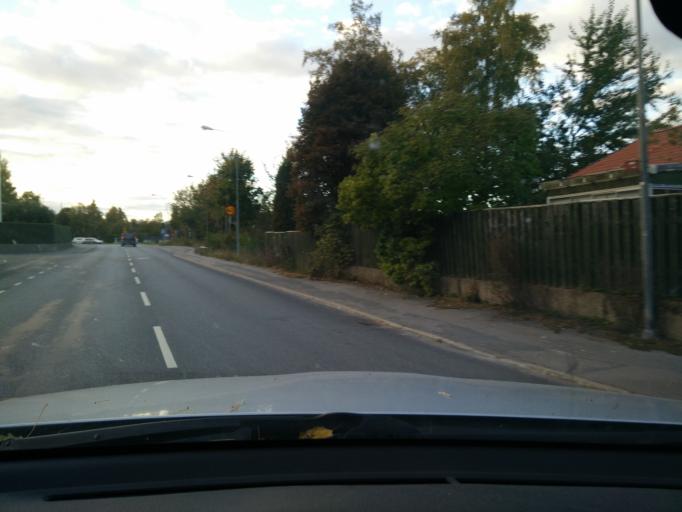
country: SE
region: Stockholm
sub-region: Sollentuna Kommun
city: Sollentuna
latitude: 59.4184
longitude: 17.9430
